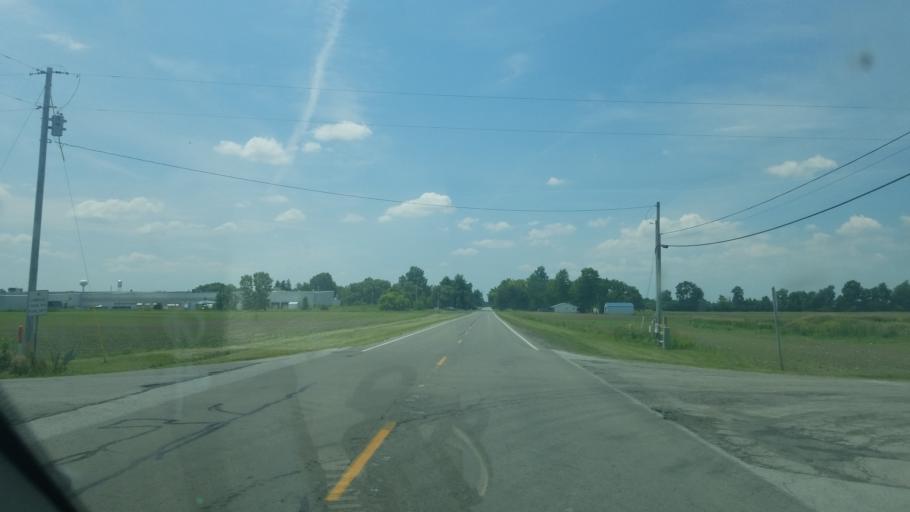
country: US
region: Ohio
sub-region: Hardin County
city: Ada
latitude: 40.7766
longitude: -83.8039
